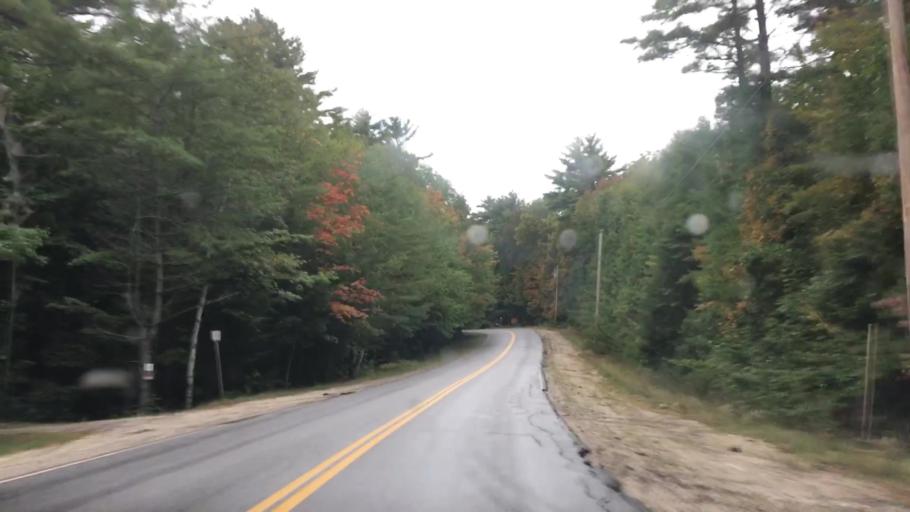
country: US
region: Maine
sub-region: Cumberland County
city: Raymond
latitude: 43.9315
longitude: -70.4085
